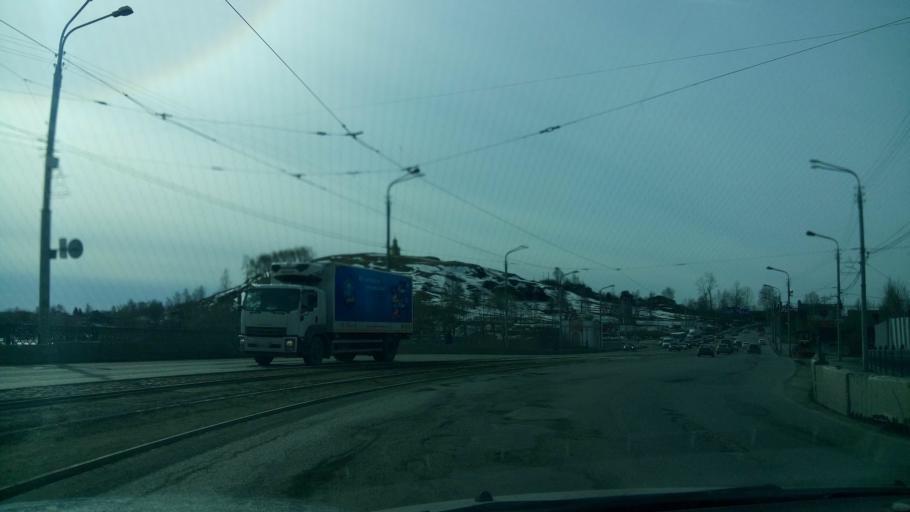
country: RU
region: Sverdlovsk
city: Nizhniy Tagil
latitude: 57.9045
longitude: 59.9499
